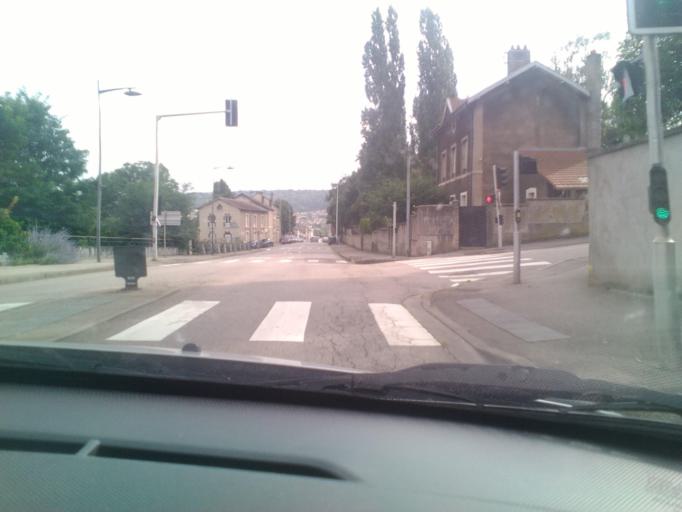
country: FR
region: Lorraine
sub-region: Departement de Meurthe-et-Moselle
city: Pompey
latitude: 48.7725
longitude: 6.1299
